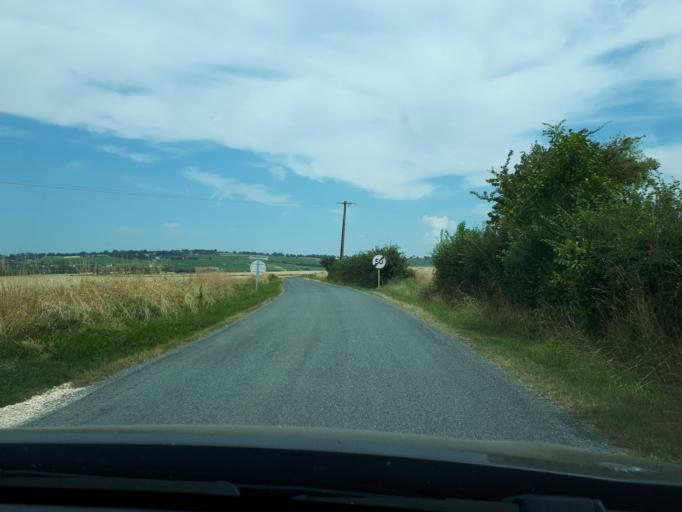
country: FR
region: Centre
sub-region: Departement du Cher
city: Sancerre
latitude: 47.2885
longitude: 2.7552
